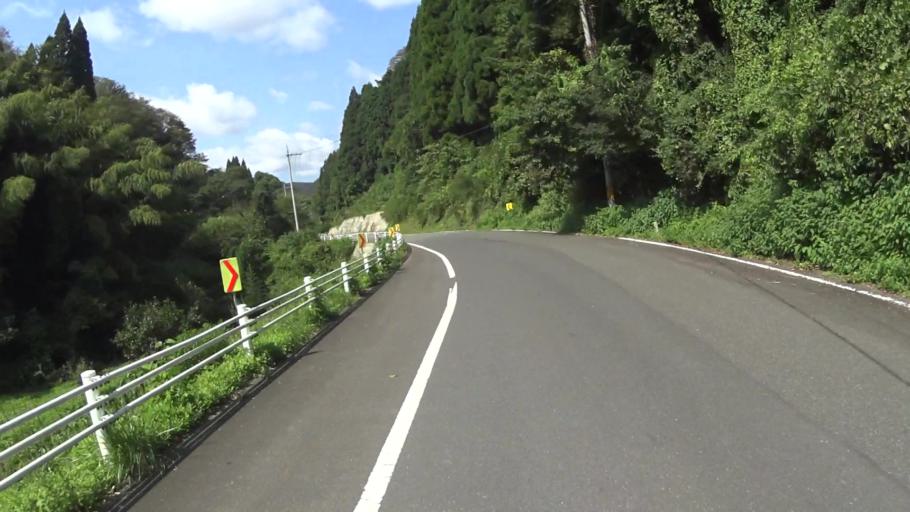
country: JP
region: Kyoto
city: Miyazu
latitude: 35.6842
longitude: 135.2612
